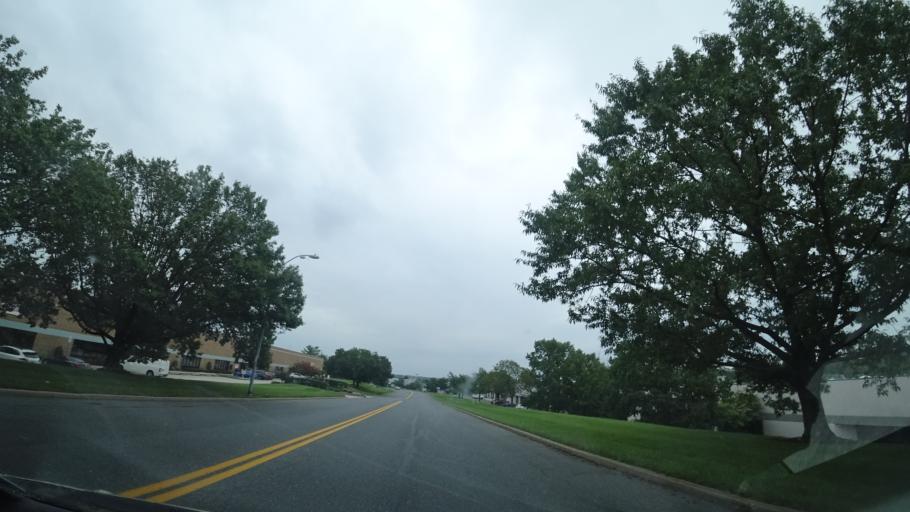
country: US
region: Maryland
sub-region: Anne Arundel County
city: Jessup
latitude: 39.1468
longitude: -76.7962
